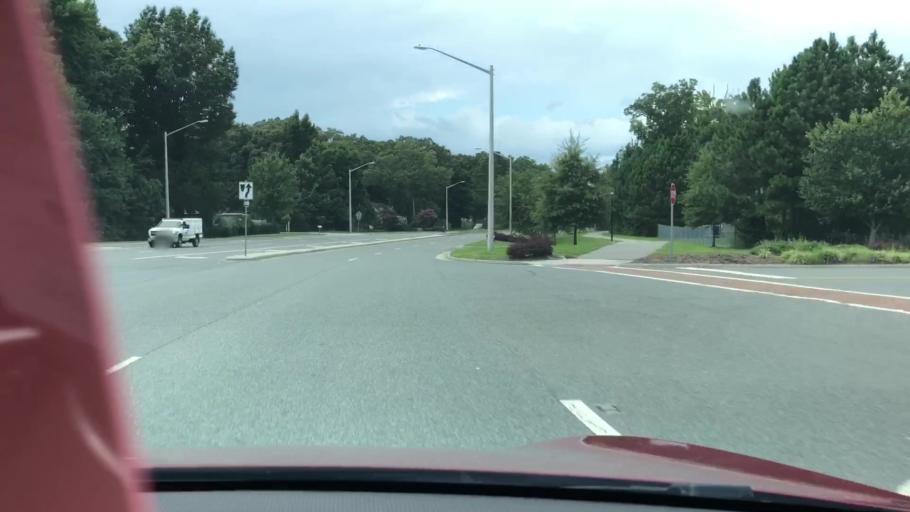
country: US
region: Virginia
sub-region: City of Virginia Beach
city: Virginia Beach
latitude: 36.8117
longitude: -75.9937
